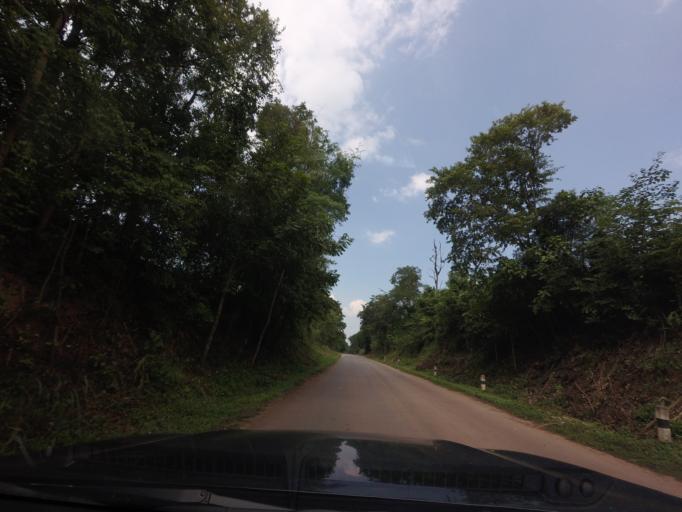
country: TH
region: Uttaradit
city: Fak Tha
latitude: 17.8371
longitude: 100.9443
